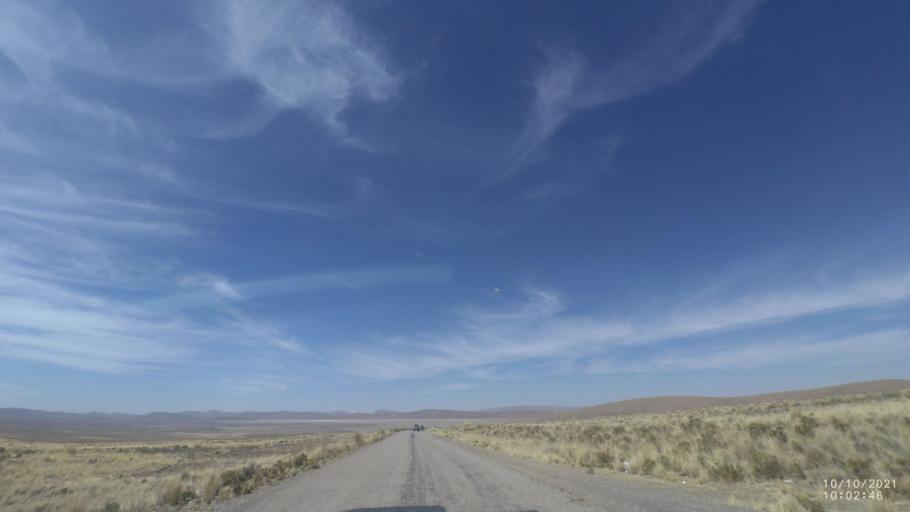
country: BO
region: La Paz
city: Eucaliptus
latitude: -17.3606
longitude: -67.4367
